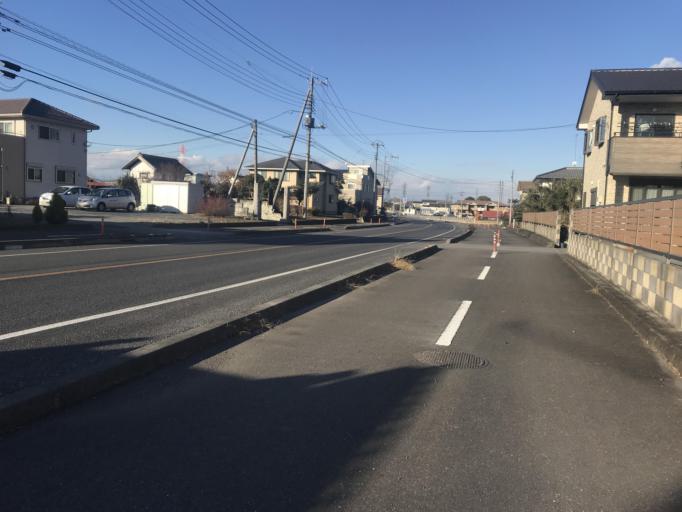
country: JP
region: Tochigi
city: Kaminokawa
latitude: 36.4319
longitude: 139.8718
